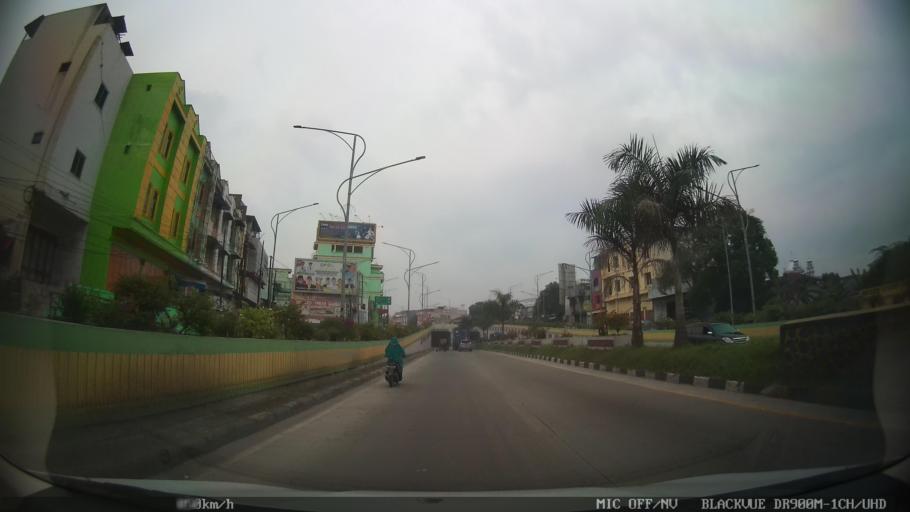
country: ID
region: North Sumatra
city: Deli Tua
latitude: 3.5395
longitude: 98.6829
